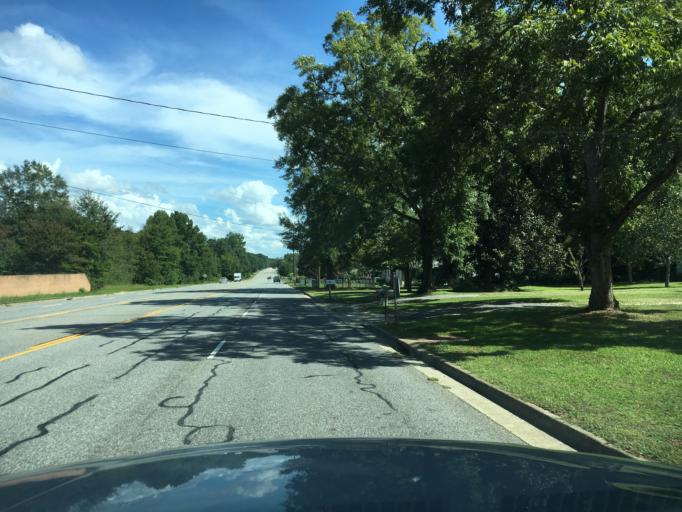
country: US
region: South Carolina
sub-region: Greenwood County
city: Ware Shoals
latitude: 34.4393
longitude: -82.2495
